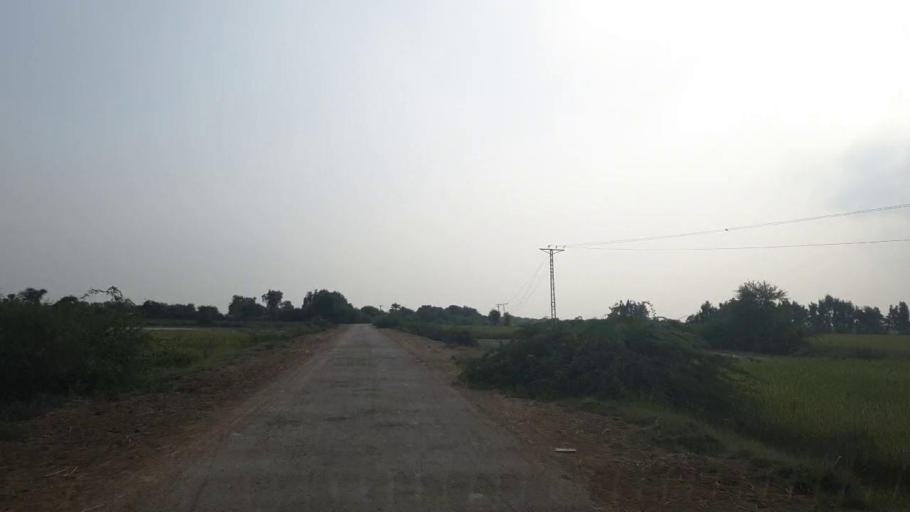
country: PK
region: Sindh
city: Badin
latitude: 24.6409
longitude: 68.6939
